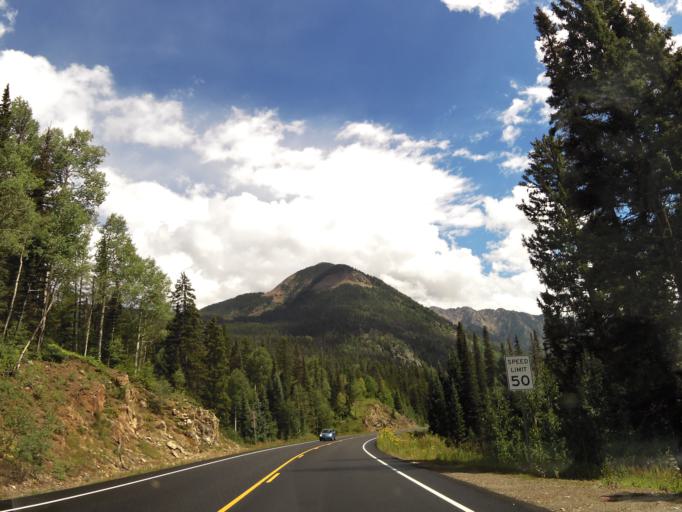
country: US
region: Colorado
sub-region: San Juan County
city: Silverton
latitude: 37.6774
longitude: -107.7945
